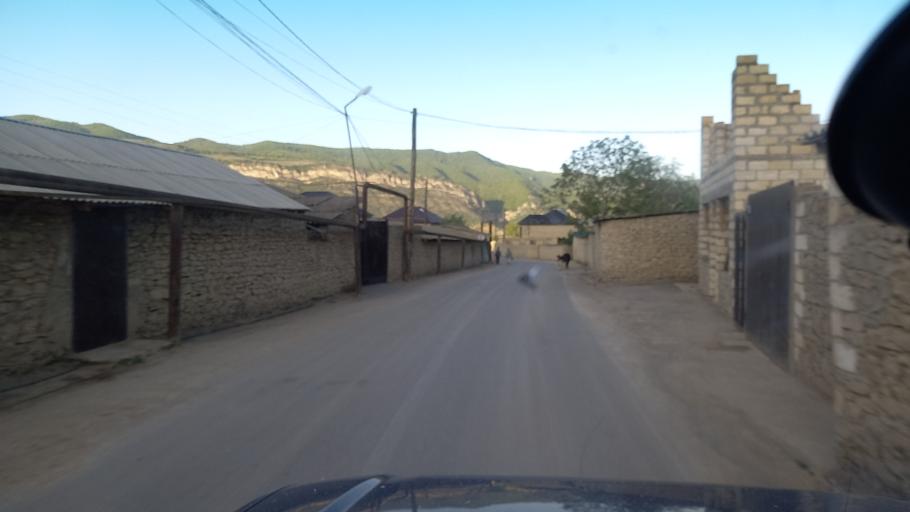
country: RU
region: Dagestan
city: Khuchni
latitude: 41.9742
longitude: 47.8917
